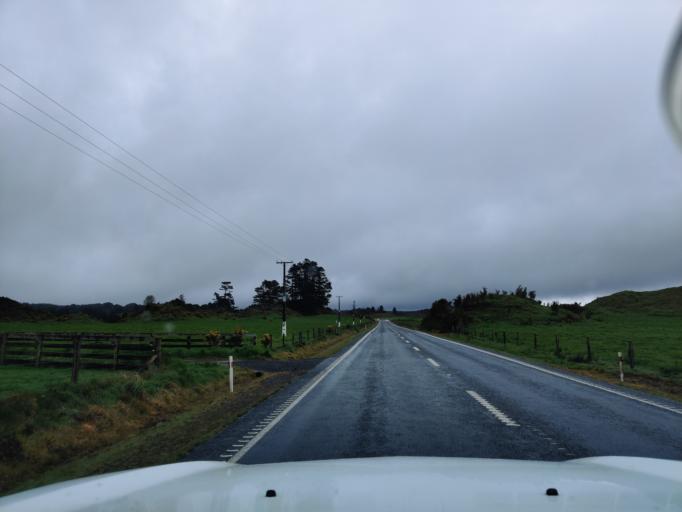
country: NZ
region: Bay of Plenty
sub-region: Rotorua District
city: Rotorua
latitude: -38.0477
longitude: 176.0726
